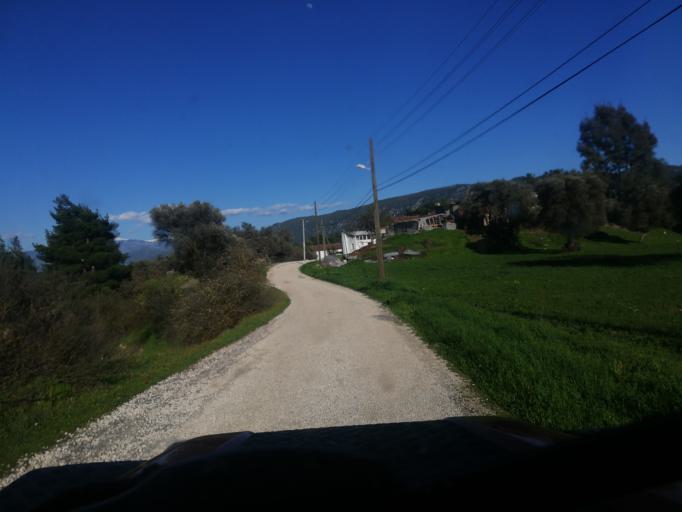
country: TR
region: Antalya
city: Kas
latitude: 36.2898
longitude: 29.7101
